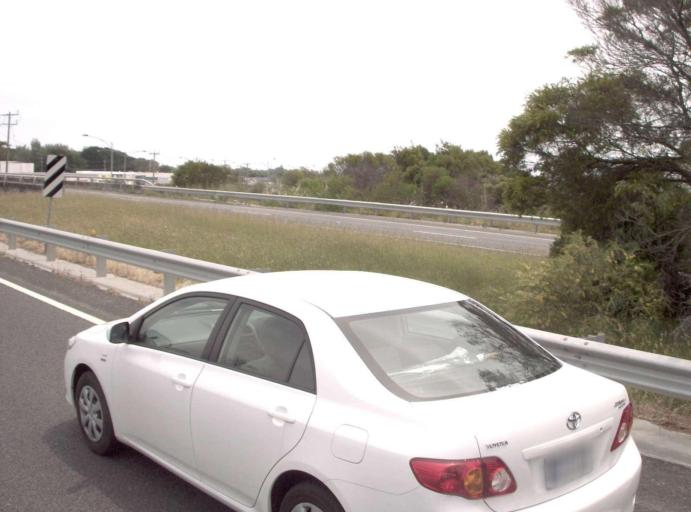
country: AU
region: Victoria
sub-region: Mornington Peninsula
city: Safety Beach
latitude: -38.3296
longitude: 144.9898
